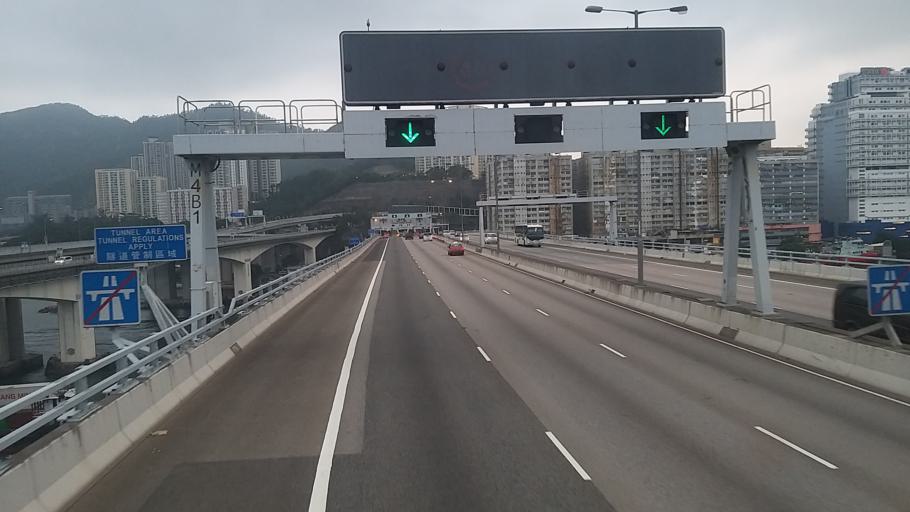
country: HK
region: Tsuen Wan
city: Tsuen Wan
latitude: 22.3499
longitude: 114.1151
